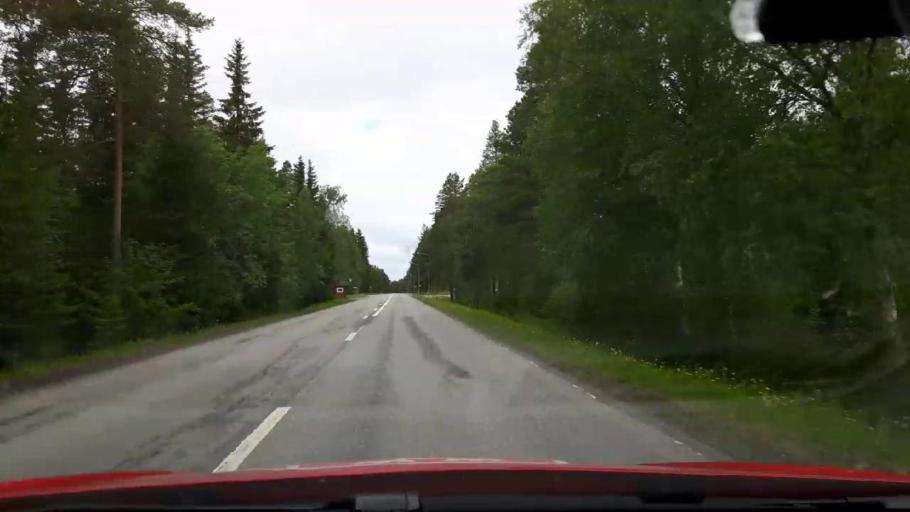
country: SE
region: Jaemtland
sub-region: Krokoms Kommun
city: Krokom
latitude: 63.2945
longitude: 14.4881
